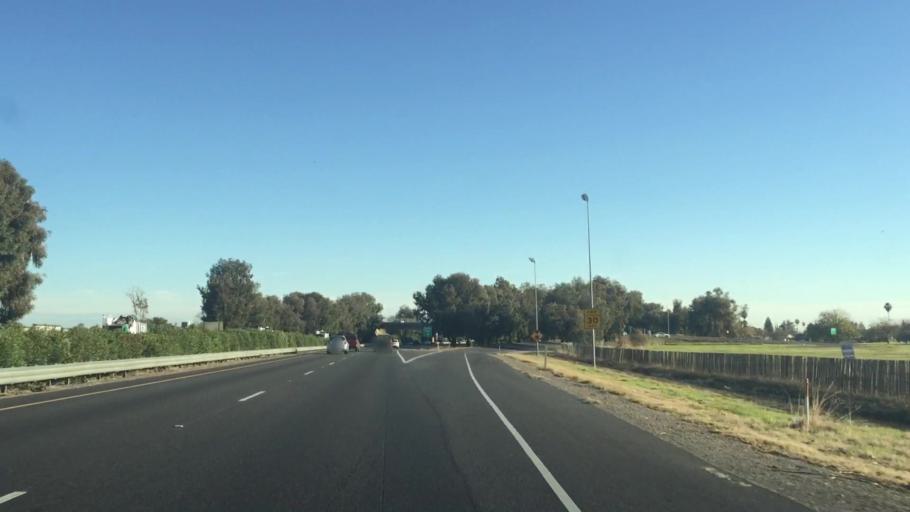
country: US
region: California
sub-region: Yuba County
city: Linda
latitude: 39.1155
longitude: -121.5625
